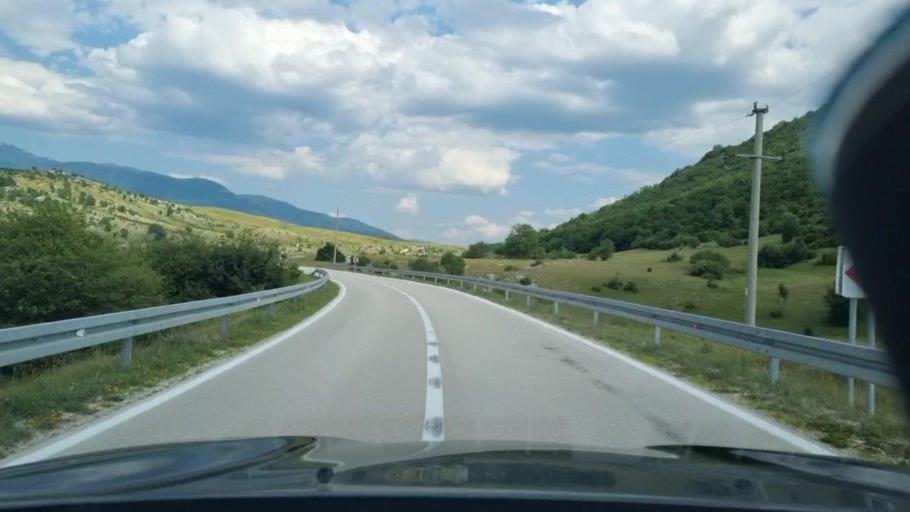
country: BA
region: Federation of Bosnia and Herzegovina
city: Bosansko Grahovo
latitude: 44.1319
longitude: 16.4804
